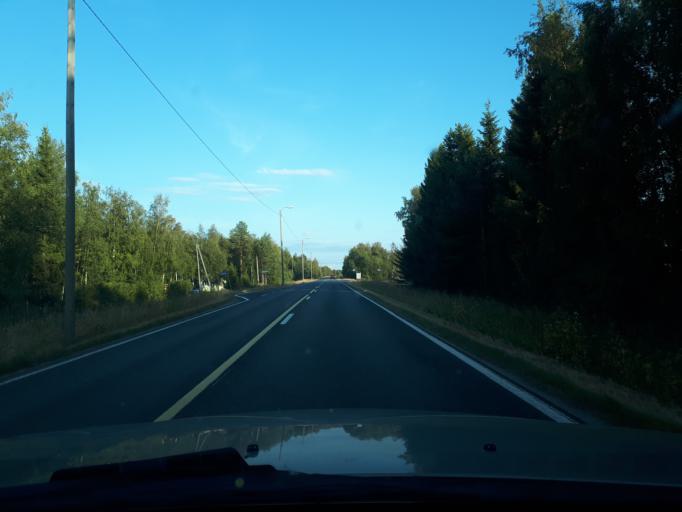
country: FI
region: Northern Ostrobothnia
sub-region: Oulu
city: Oulunsalo
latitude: 64.9862
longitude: 25.2621
